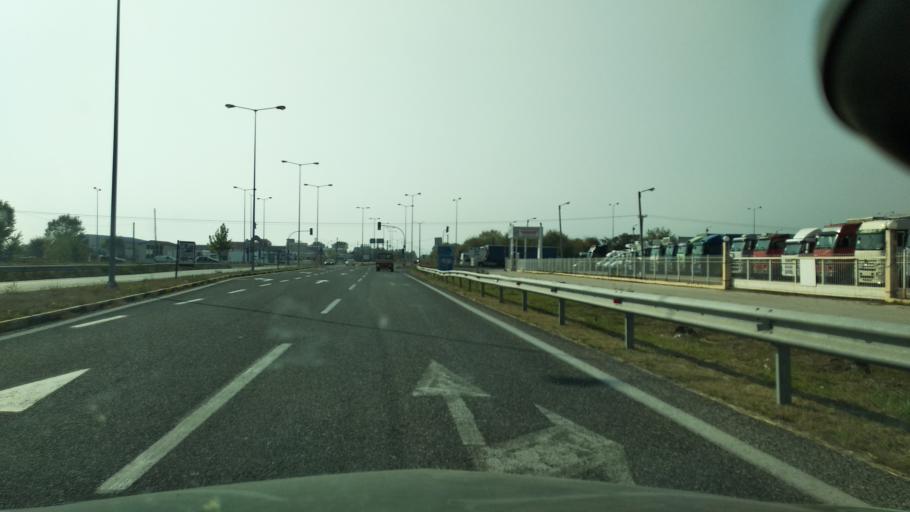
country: GR
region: Thessaly
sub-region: Trikala
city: Trikala
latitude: 39.5575
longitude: 21.8021
